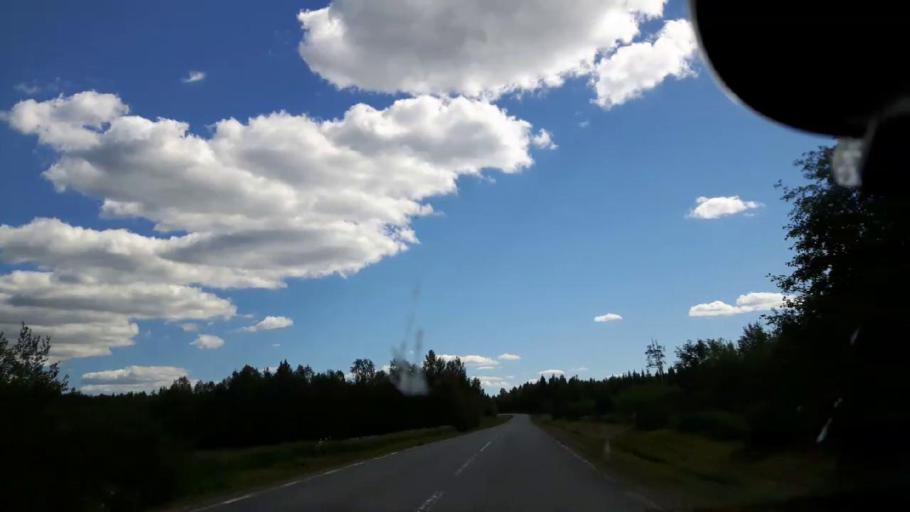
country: SE
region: Jaemtland
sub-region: Ragunda Kommun
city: Hammarstrand
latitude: 62.8299
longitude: 16.1846
